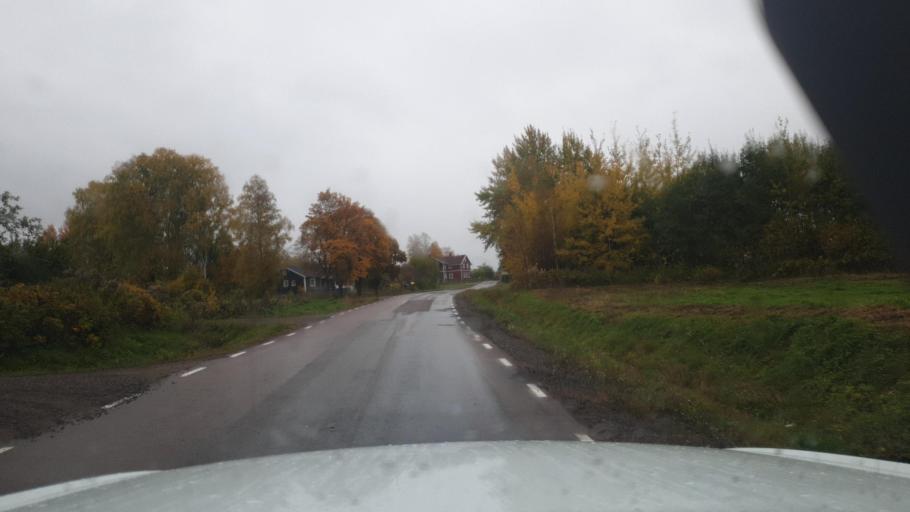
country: SE
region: Vaermland
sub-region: Eda Kommun
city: Charlottenberg
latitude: 59.8315
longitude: 12.3251
